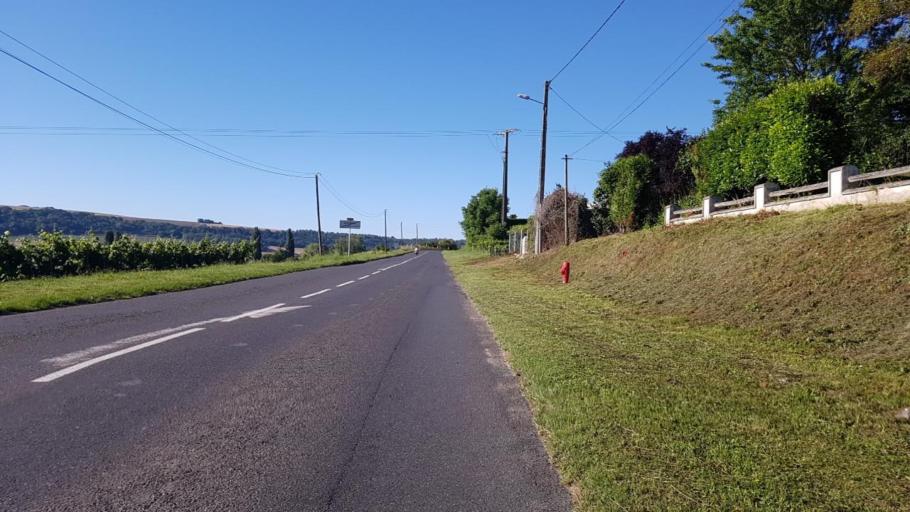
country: FR
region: Picardie
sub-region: Departement de l'Aisne
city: Essomes-sur-Marne
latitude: 49.0124
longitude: 3.3754
